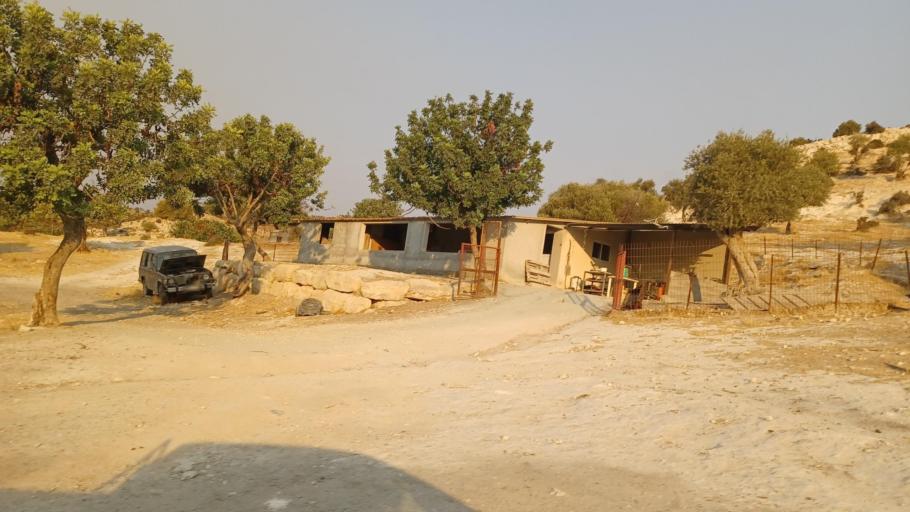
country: CY
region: Limassol
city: Pissouri
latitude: 34.7043
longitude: 32.6667
